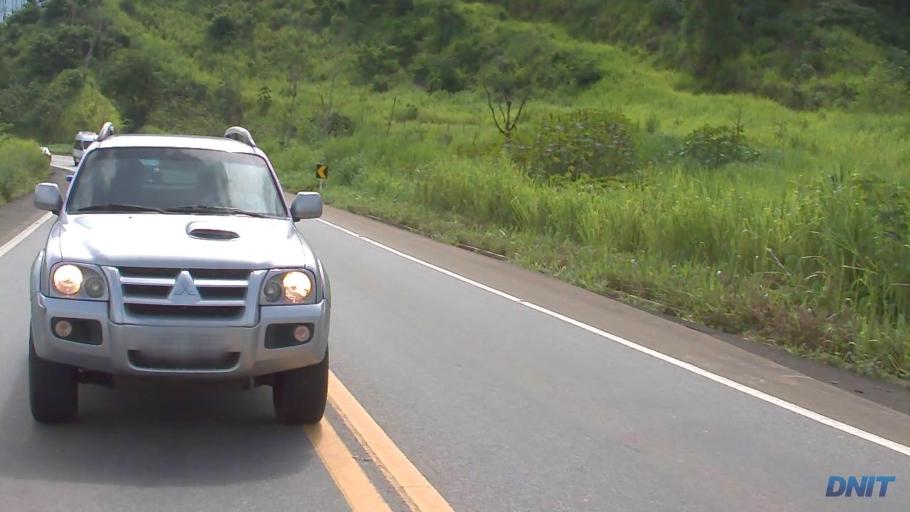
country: BR
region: Minas Gerais
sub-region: Ipaba
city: Ipaba
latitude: -19.3675
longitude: -42.4508
